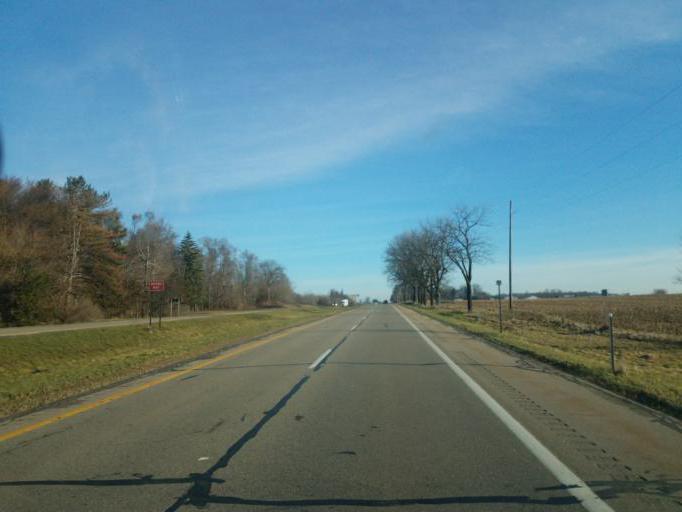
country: US
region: Michigan
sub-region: Clinton County
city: Saint Johns
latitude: 43.0532
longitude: -84.5637
